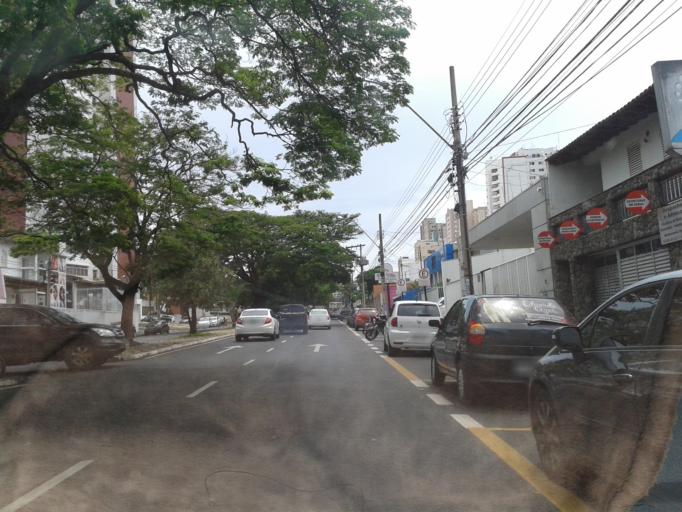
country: BR
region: Minas Gerais
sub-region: Uberlandia
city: Uberlandia
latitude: -18.9214
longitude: -48.2873
